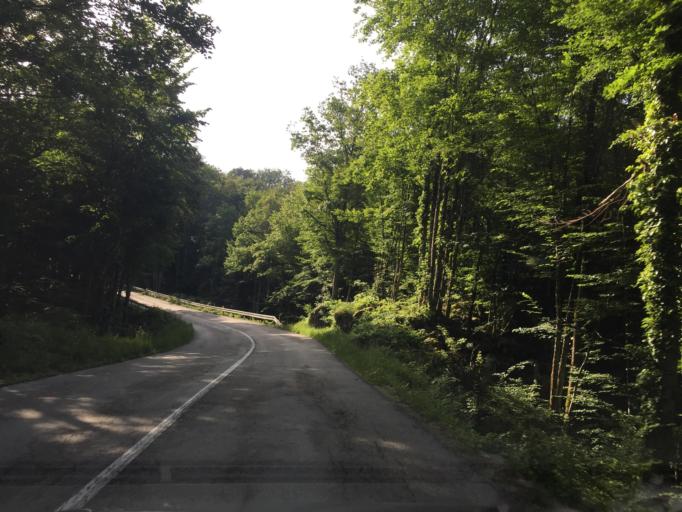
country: HR
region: Primorsko-Goranska
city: Matulji
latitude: 45.4187
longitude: 14.2284
